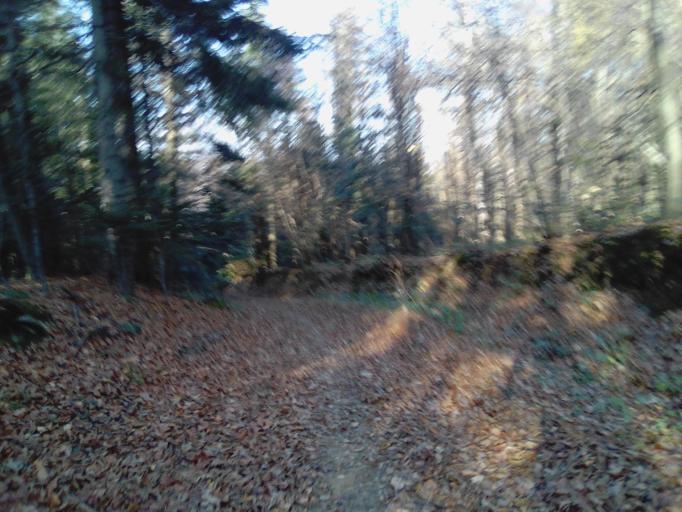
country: PL
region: Subcarpathian Voivodeship
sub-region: Powiat brzozowski
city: Domaradz
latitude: 49.7866
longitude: 21.8886
